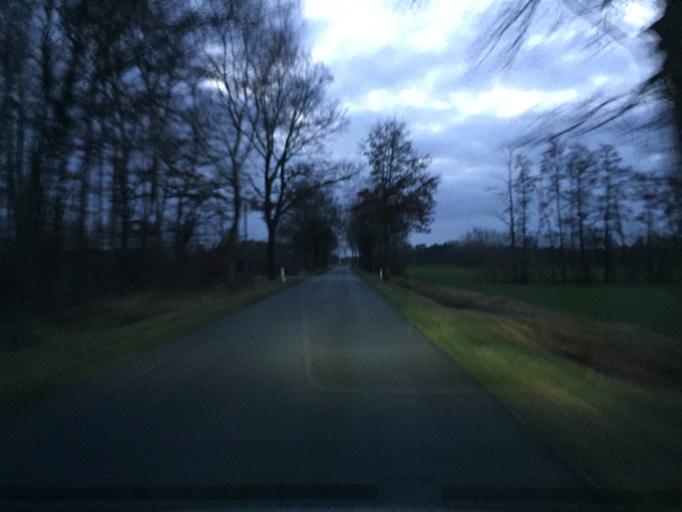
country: DE
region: Lower Saxony
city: Kirchdorf
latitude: 52.6362
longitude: 8.8447
